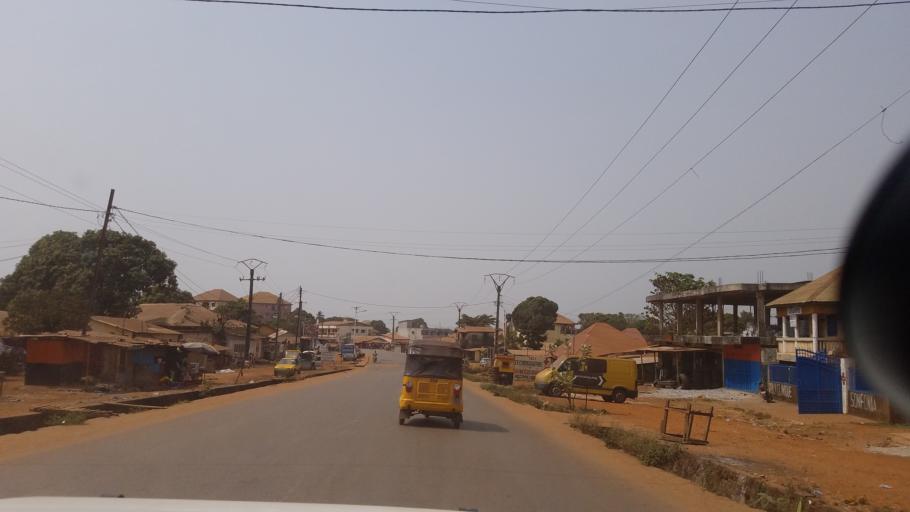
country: GN
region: Kindia
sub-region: Prefecture de Dubreka
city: Dubreka
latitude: 9.6807
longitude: -13.5695
